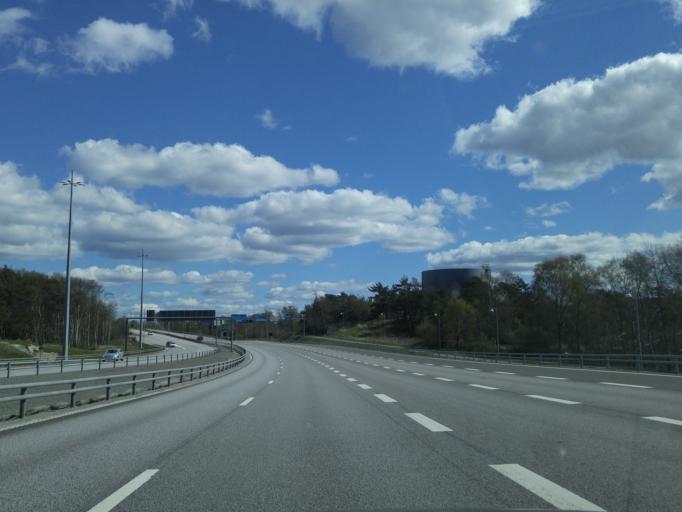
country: SE
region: Vaestra Goetaland
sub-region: Goteborg
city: Majorna
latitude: 57.7043
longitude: 11.8807
